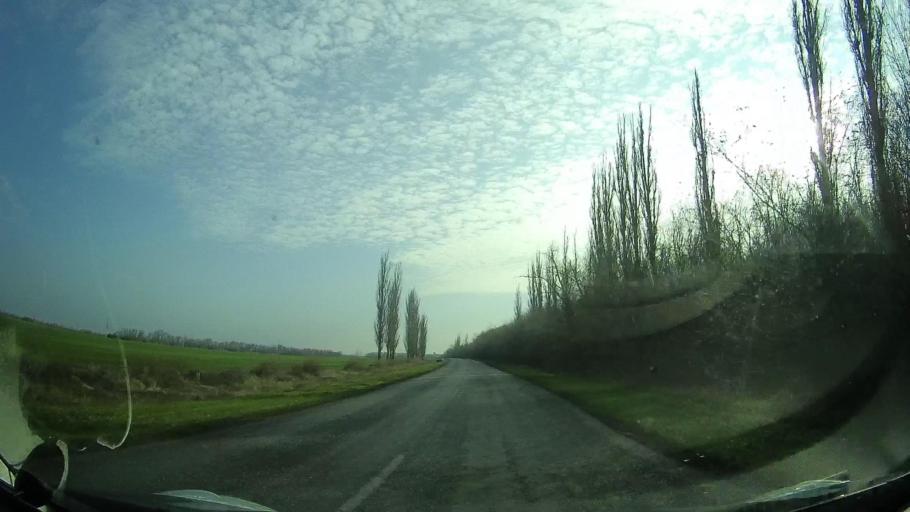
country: RU
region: Rostov
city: Mechetinskaya
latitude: 46.8228
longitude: 40.5543
